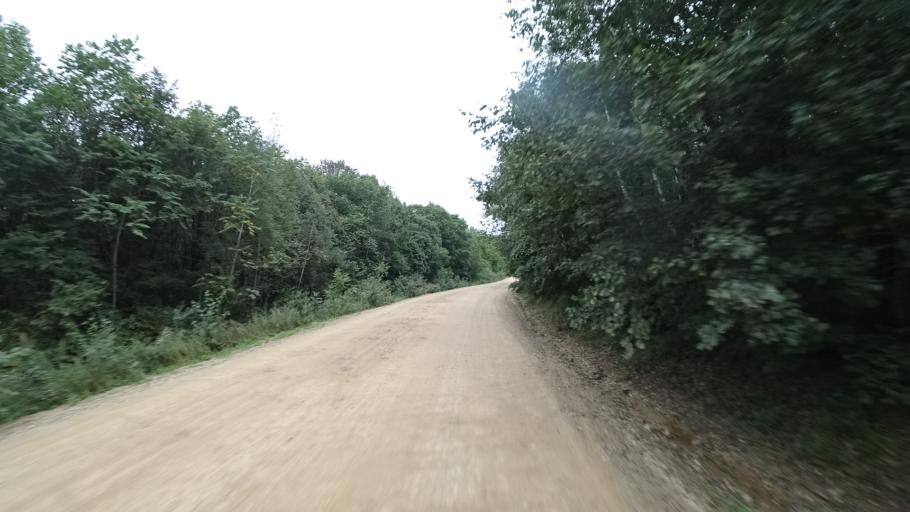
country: RU
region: Primorskiy
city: Rettikhovka
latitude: 44.1858
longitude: 132.8097
